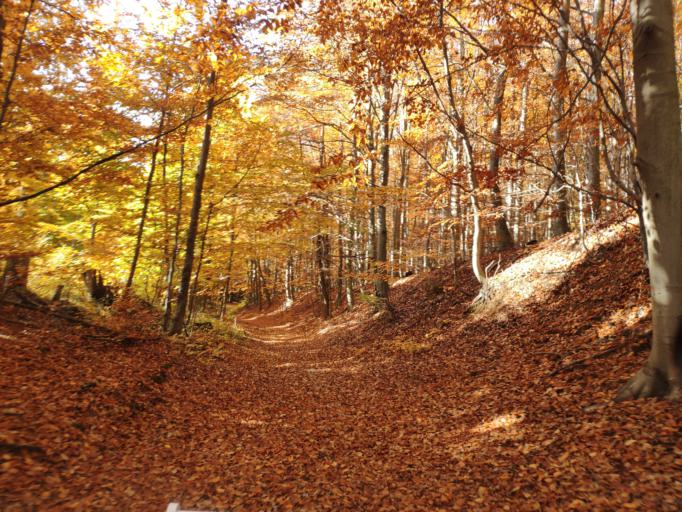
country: SK
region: Kosicky
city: Moldava nad Bodvou
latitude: 48.7223
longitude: 21.0343
